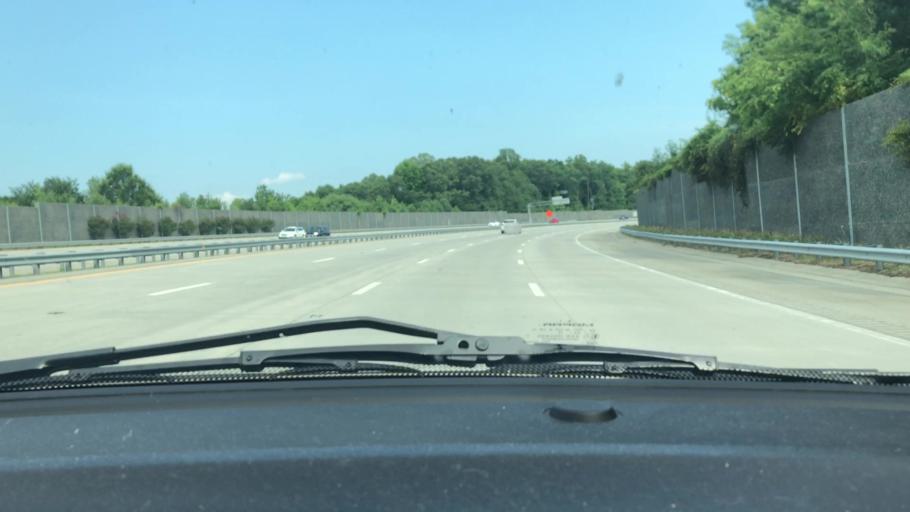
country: US
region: North Carolina
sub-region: Guilford County
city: Greensboro
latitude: 36.0199
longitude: -79.8560
